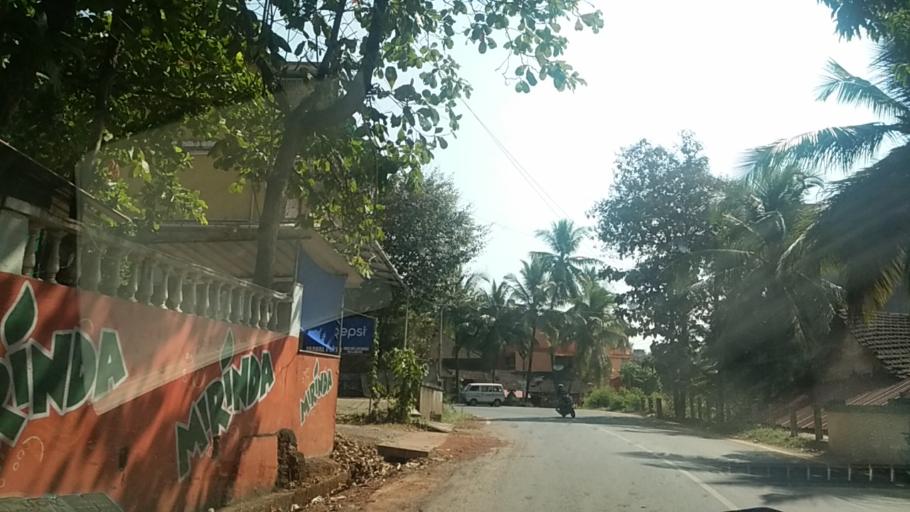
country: IN
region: Goa
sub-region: South Goa
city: Madgaon
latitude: 15.2922
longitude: 73.9564
